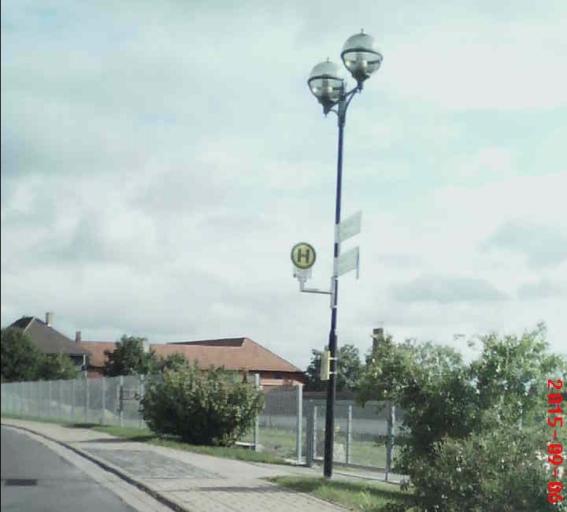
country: DE
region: Thuringia
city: Sollstedt
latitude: 51.2700
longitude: 10.4408
